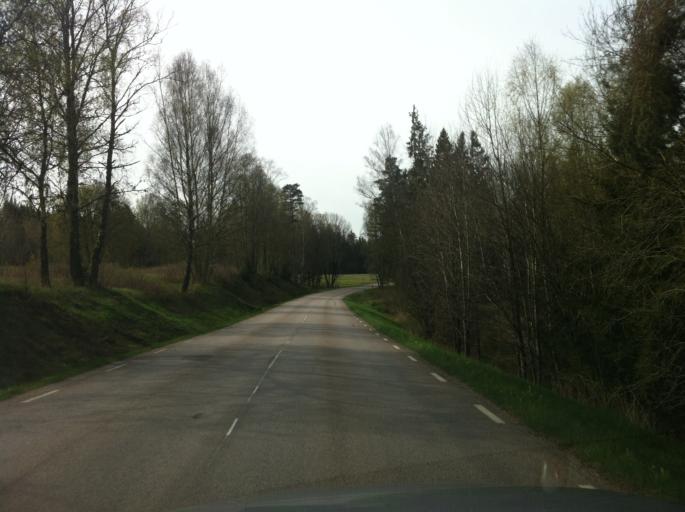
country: SE
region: Vaestra Goetaland
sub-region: Bollebygds Kommun
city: Bollebygd
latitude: 57.7182
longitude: 12.5857
